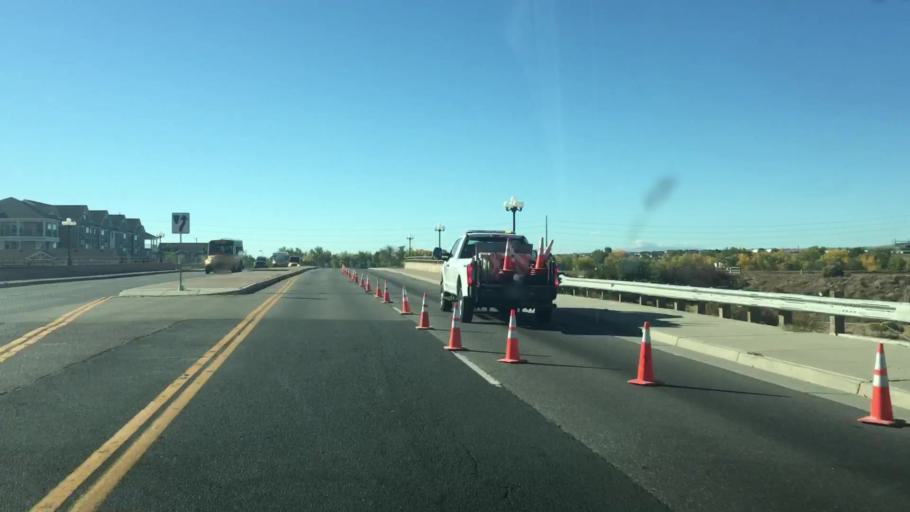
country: US
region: Colorado
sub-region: Douglas County
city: Parker
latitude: 39.5172
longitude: -104.7748
